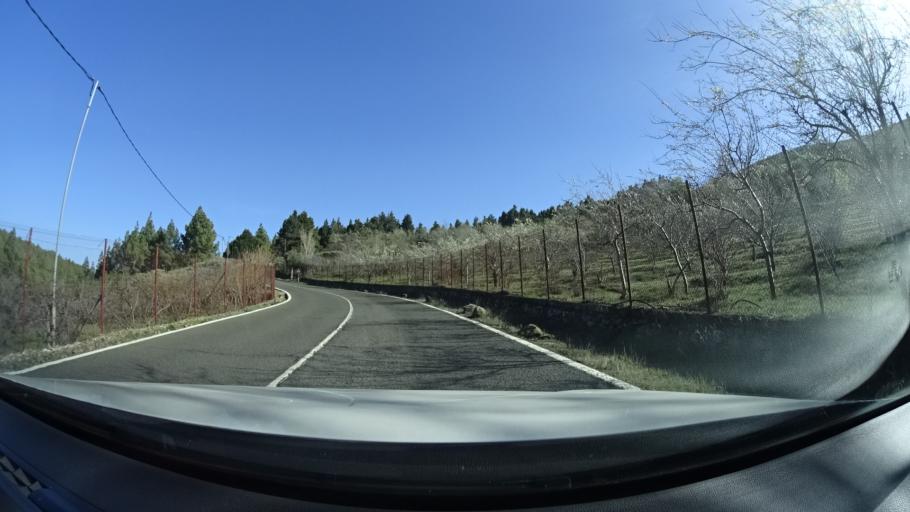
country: ES
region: Canary Islands
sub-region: Provincia de Las Palmas
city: Vega de San Mateo
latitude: 27.9665
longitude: -15.5480
